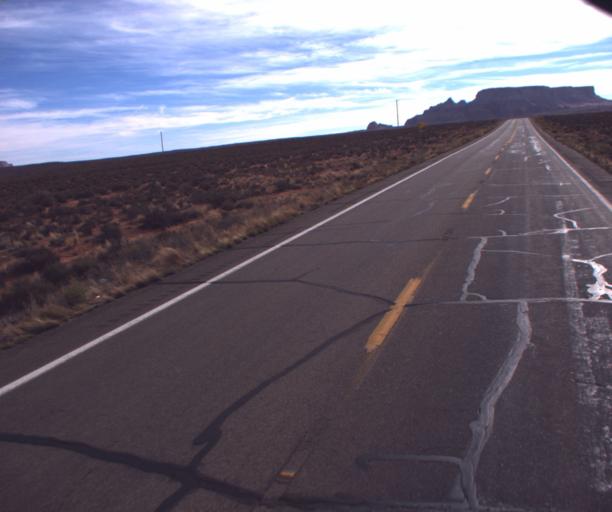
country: US
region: Arizona
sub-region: Coconino County
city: LeChee
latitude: 36.8873
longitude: -111.3628
